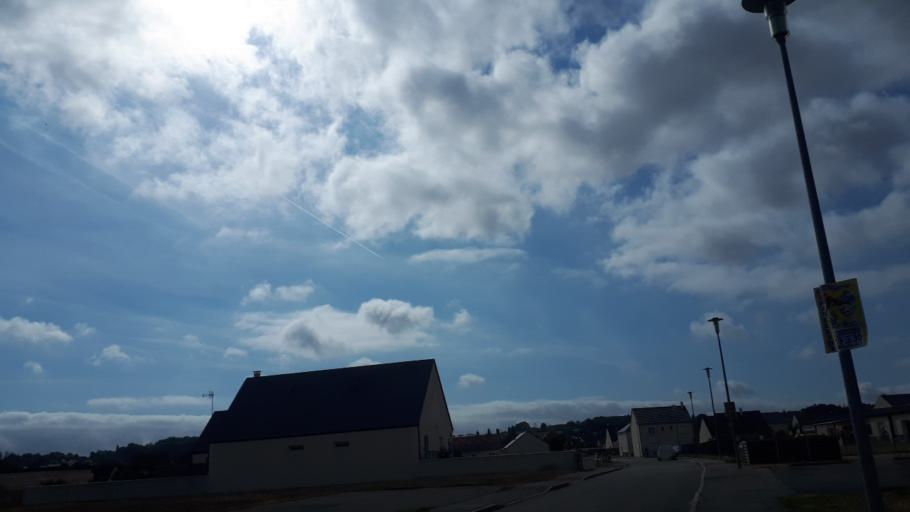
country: FR
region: Centre
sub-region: Departement du Loir-et-Cher
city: Naveil
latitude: 47.7932
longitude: 1.0389
